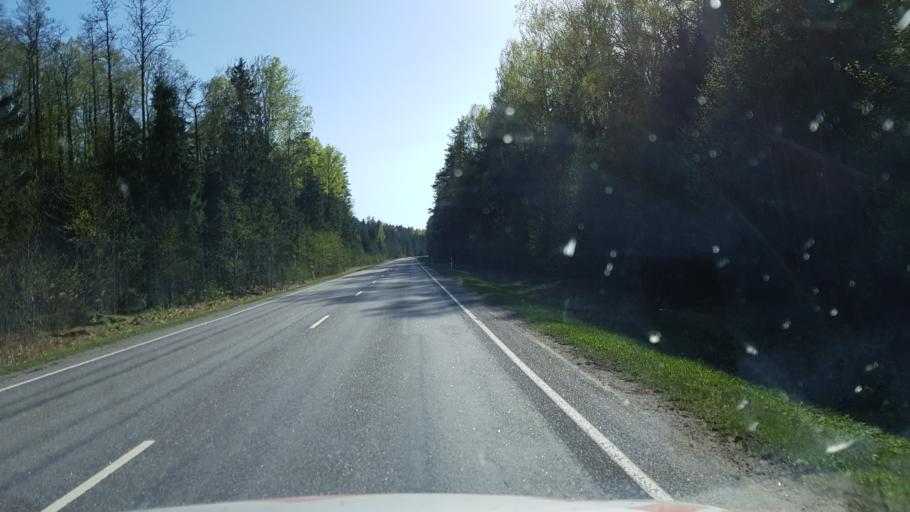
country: EE
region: Viljandimaa
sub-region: Moisakuela linn
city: Moisakula
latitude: 58.2273
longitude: 25.1103
